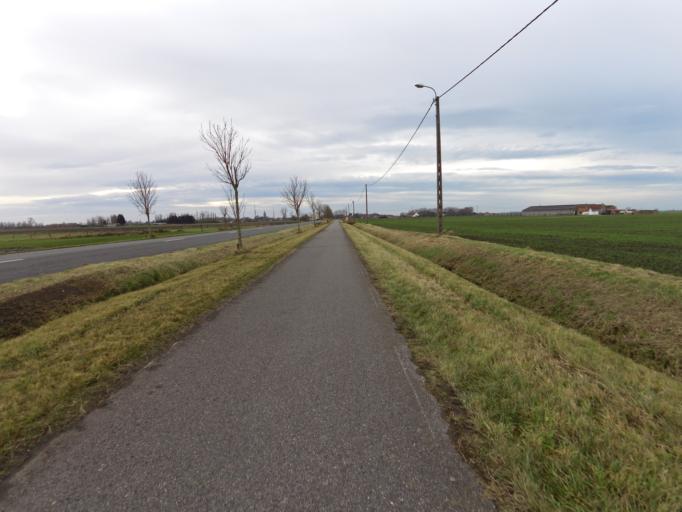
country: BE
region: Flanders
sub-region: Provincie West-Vlaanderen
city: Ostend
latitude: 51.1851
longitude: 2.8951
